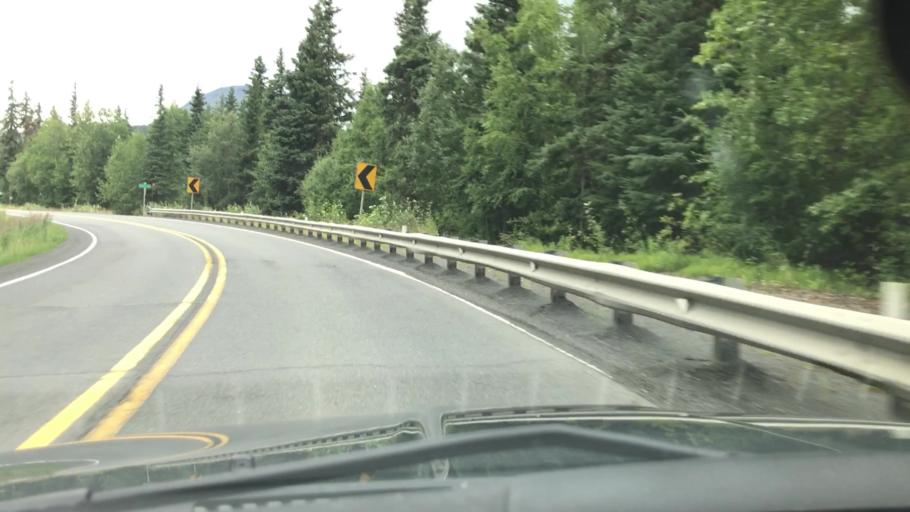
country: US
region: Alaska
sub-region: Kenai Peninsula Borough
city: Seward
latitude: 60.4865
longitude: -149.8575
